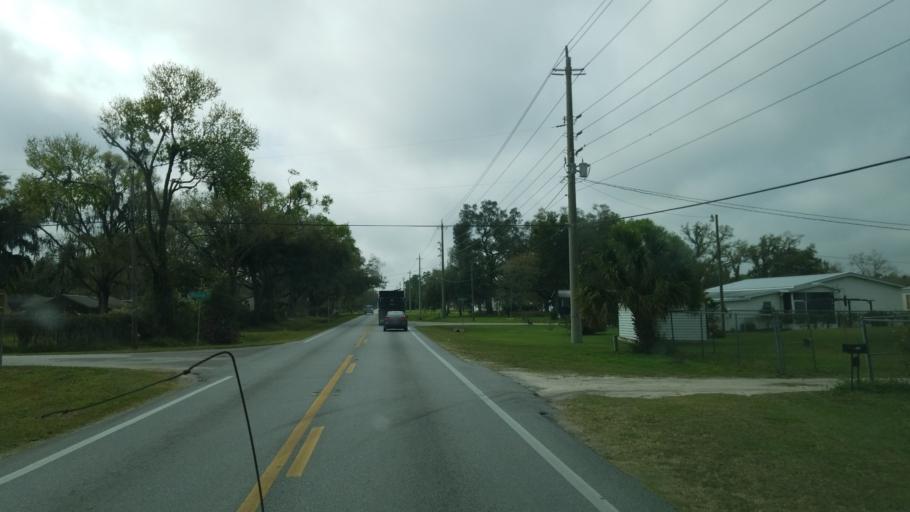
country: US
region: Florida
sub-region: Polk County
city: Winston
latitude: 28.0772
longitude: -82.0067
